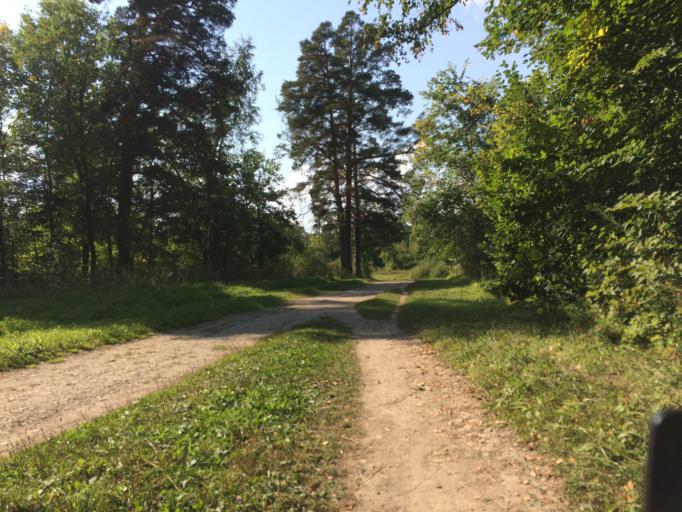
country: RU
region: Mariy-El
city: Yoshkar-Ola
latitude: 56.6178
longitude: 47.9334
